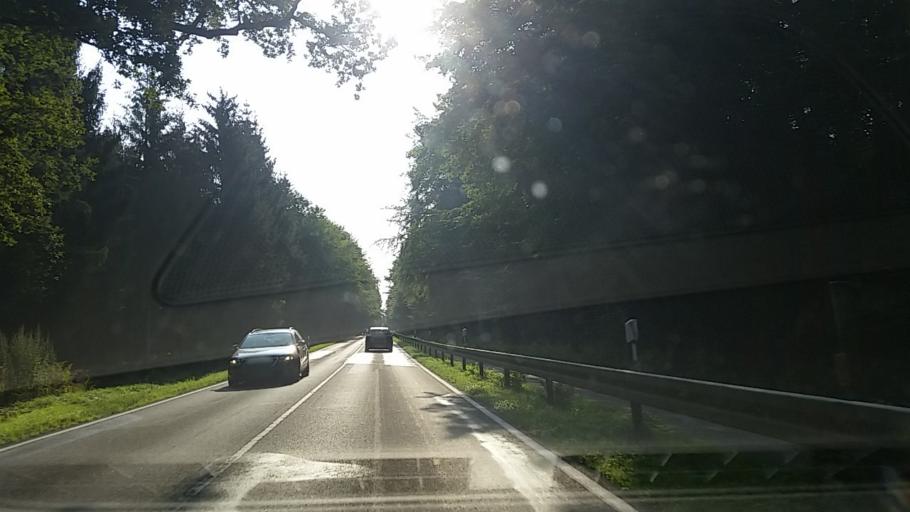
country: DE
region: Mecklenburg-Vorpommern
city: Wittenburg
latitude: 53.4839
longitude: 11.1136
